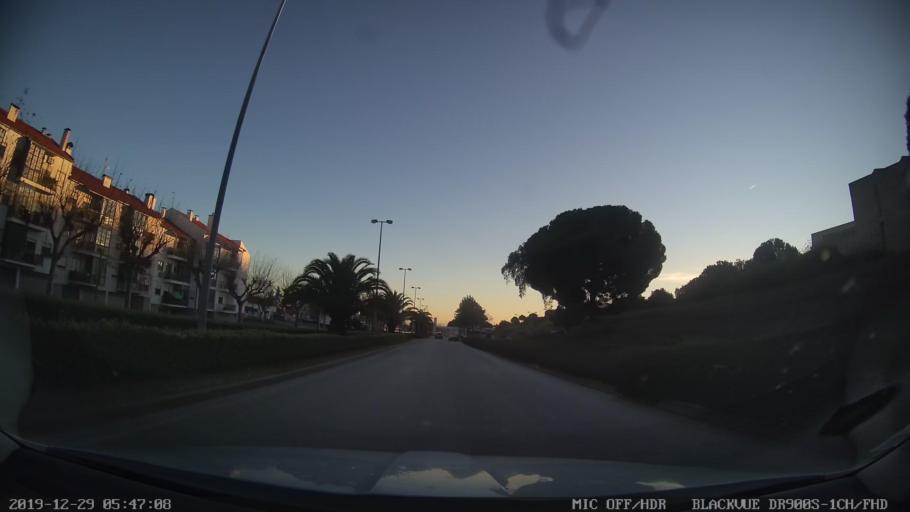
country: PT
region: Castelo Branco
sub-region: Idanha-A-Nova
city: Idanha-a-Nova
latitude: 39.9268
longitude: -7.2436
